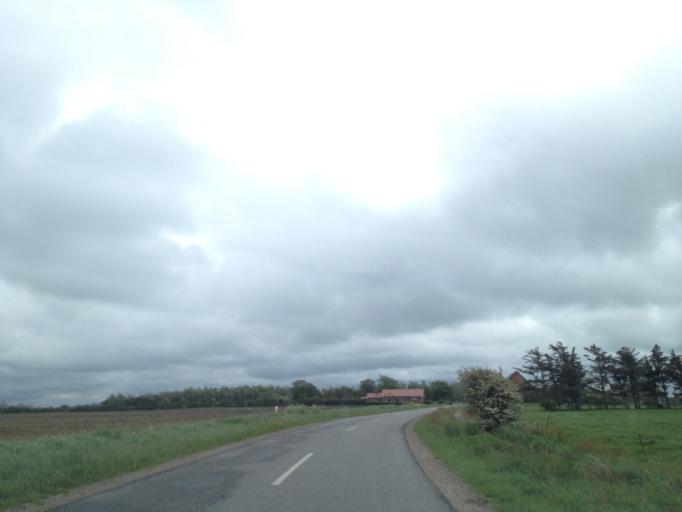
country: DK
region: South Denmark
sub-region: Tonder Kommune
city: Sherrebek
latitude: 55.1005
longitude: 8.7384
